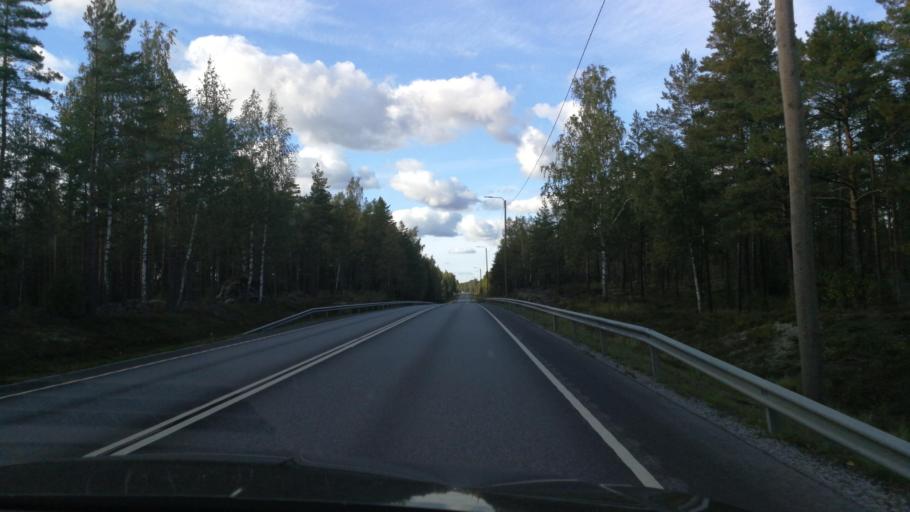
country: FI
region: Varsinais-Suomi
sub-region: Turku
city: Mynaemaeki
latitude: 60.7707
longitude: 21.8935
